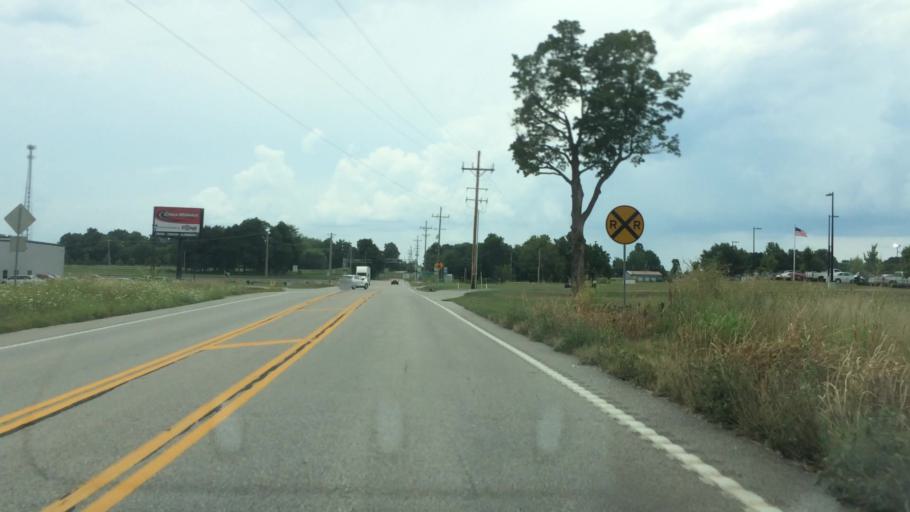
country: US
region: Missouri
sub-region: Greene County
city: Strafford
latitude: 37.2624
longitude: -93.1352
